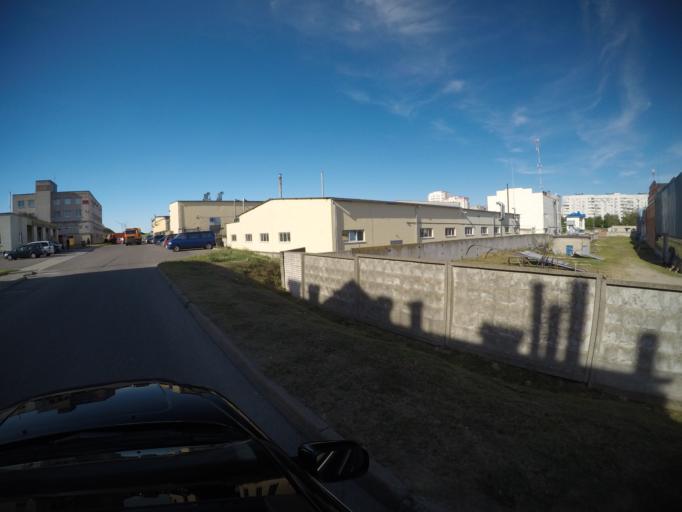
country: BY
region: Grodnenskaya
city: Hrodna
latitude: 53.7117
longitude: 23.8363
